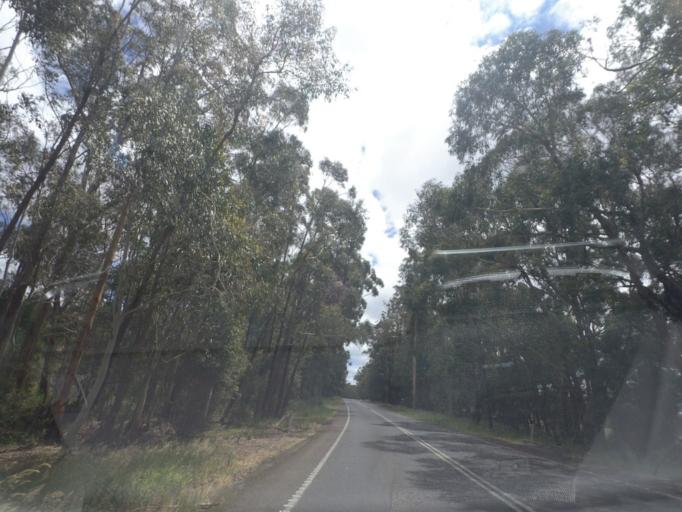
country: AU
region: Victoria
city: Brown Hill
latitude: -37.4842
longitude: 144.1531
